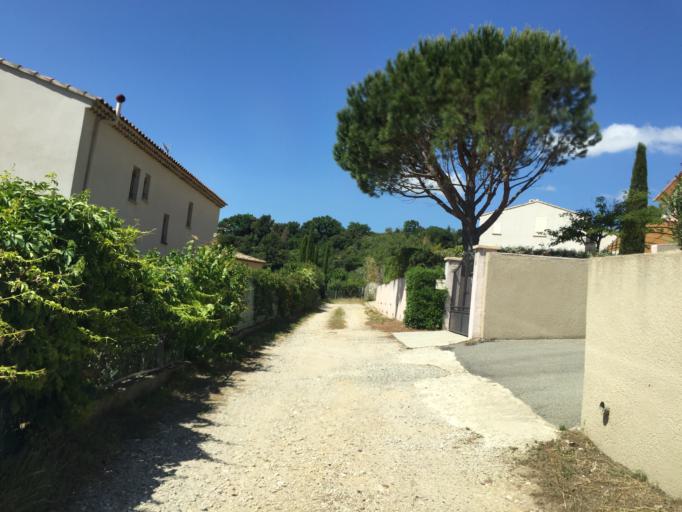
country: FR
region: Provence-Alpes-Cote d'Azur
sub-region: Departement du Vaucluse
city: Bedarrides
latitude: 44.0438
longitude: 4.8794
